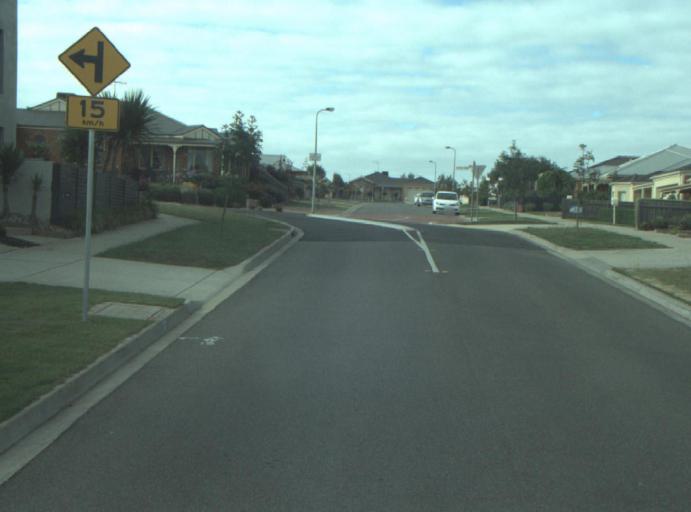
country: AU
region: Victoria
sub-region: Greater Geelong
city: Wandana Heights
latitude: -38.2088
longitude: 144.3130
